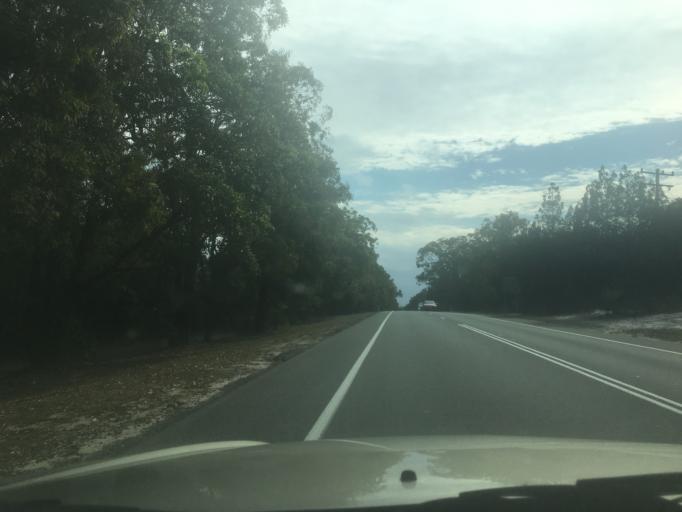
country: AU
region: Queensland
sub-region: Moreton Bay
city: Woorim
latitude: -27.0737
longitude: 153.1931
